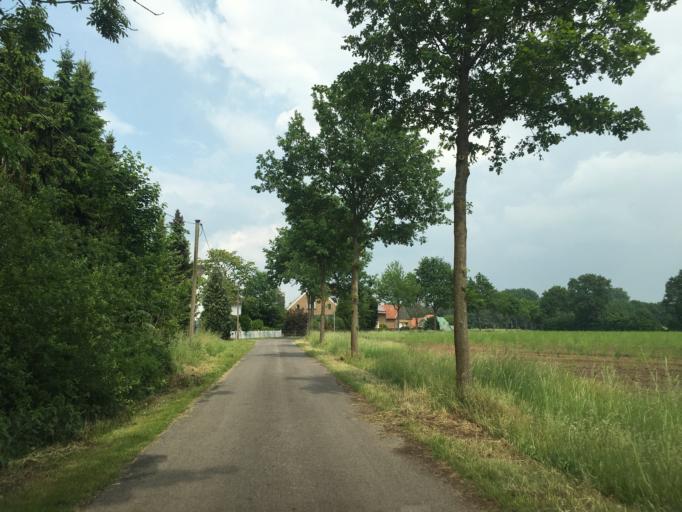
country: DE
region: North Rhine-Westphalia
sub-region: Regierungsbezirk Munster
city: Greven
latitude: 52.0408
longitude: 7.5972
